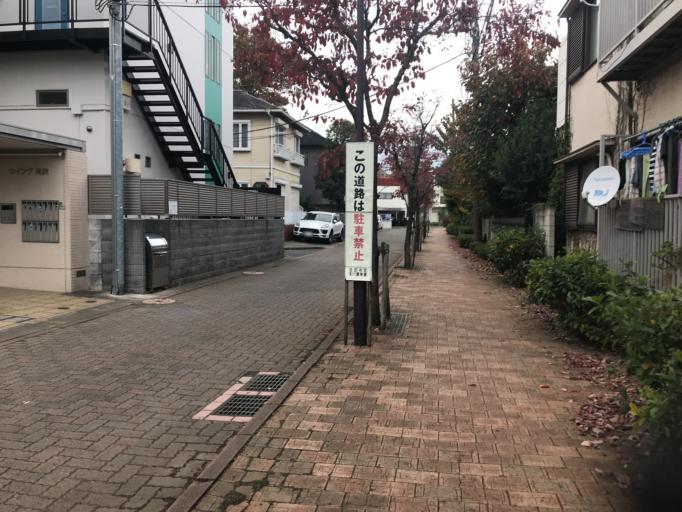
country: JP
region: Tokyo
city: Tokyo
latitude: 35.6090
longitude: 139.6626
